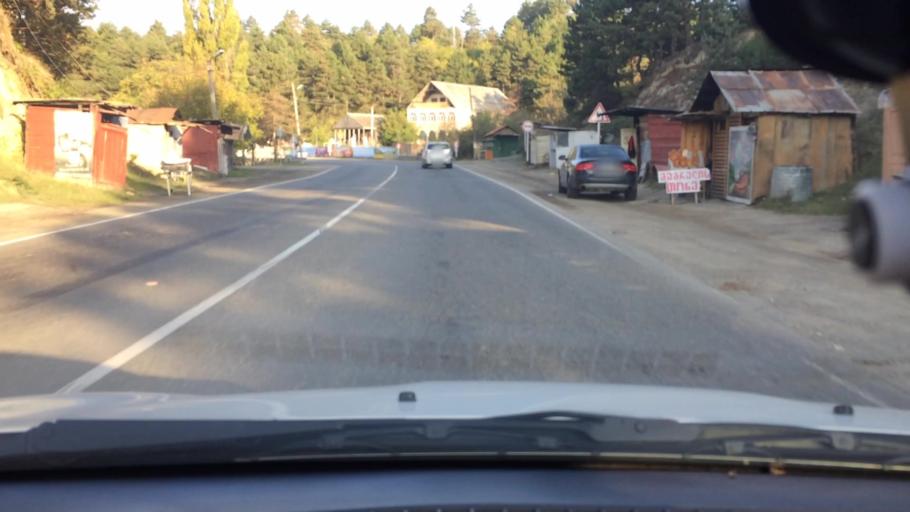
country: GE
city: Surami
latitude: 42.0273
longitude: 43.5603
